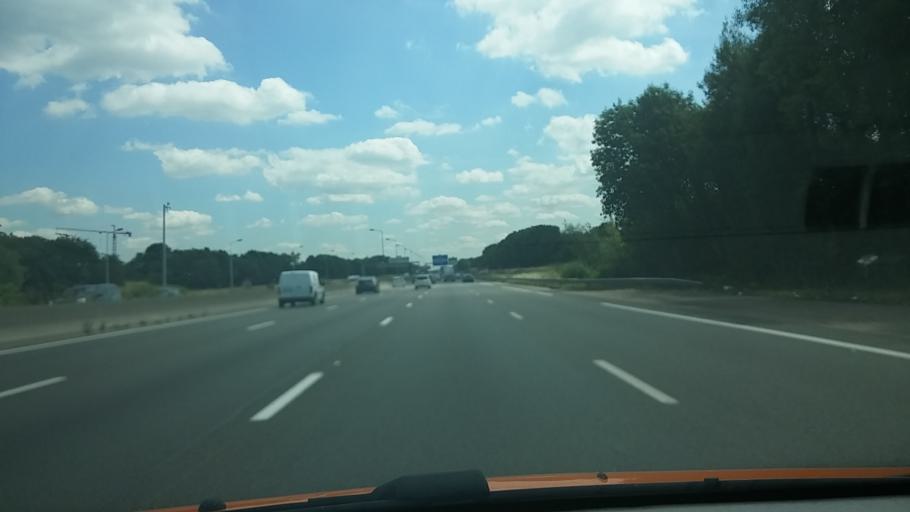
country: FR
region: Ile-de-France
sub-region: Departement de Seine-Saint-Denis
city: Noisy-le-Grand
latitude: 48.8356
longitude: 2.5642
